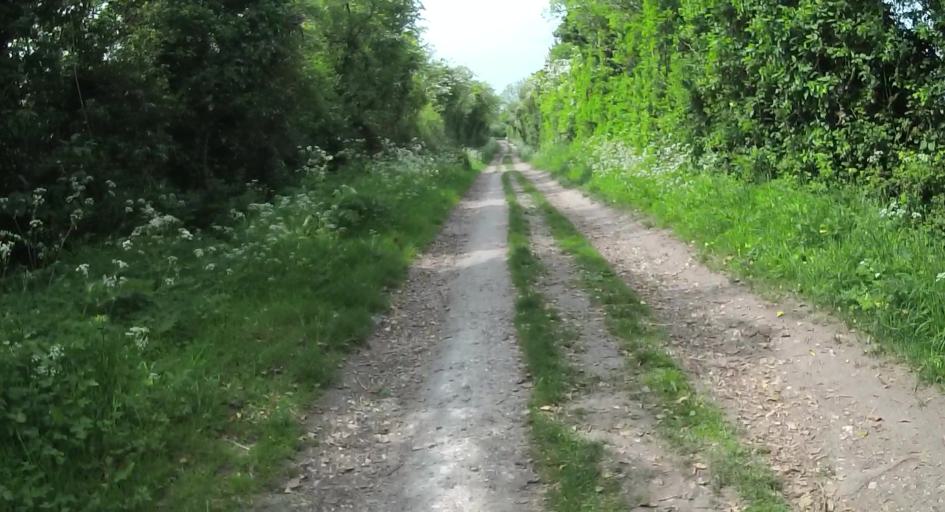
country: GB
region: England
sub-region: Hampshire
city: Kingsclere
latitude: 51.3203
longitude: -1.2363
